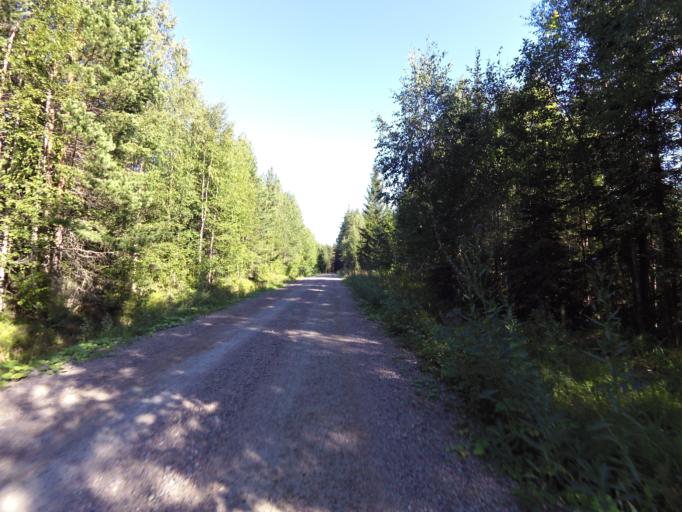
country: SE
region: Gaevleborg
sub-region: Hofors Kommun
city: Hofors
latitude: 60.6450
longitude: 16.2754
